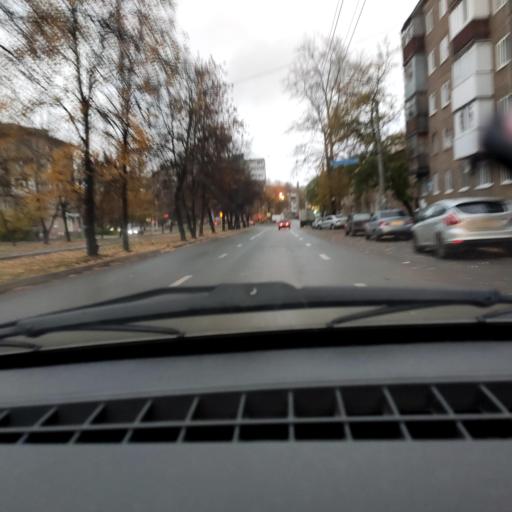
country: RU
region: Bashkortostan
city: Ufa
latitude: 54.8115
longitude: 56.1153
